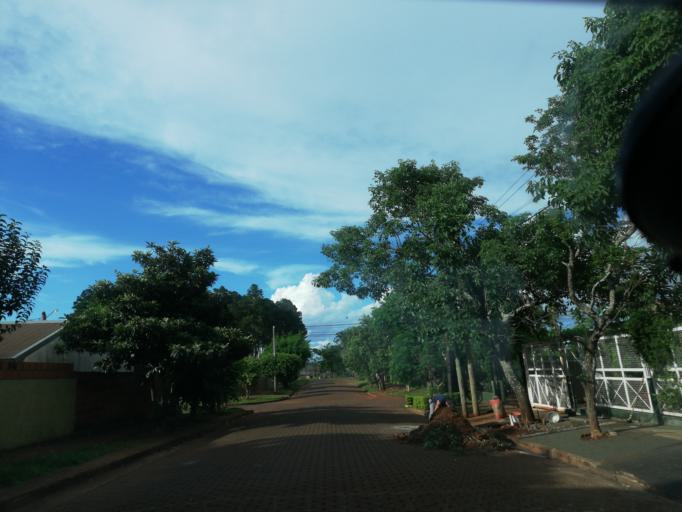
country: AR
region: Misiones
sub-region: Departamento de Capital
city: Posadas
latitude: -27.4183
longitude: -55.9529
